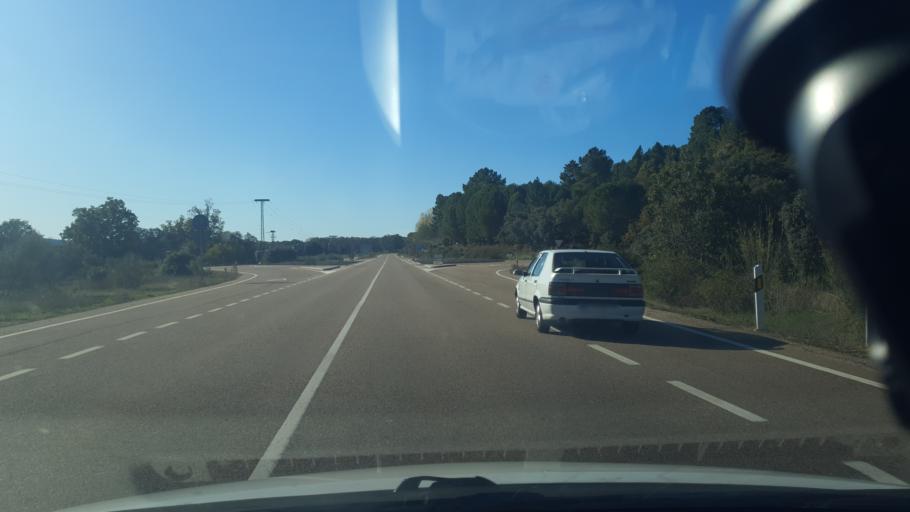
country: ES
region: Castille and Leon
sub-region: Provincia de Avila
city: Arenas de San Pedro
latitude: 40.1805
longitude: -5.0869
